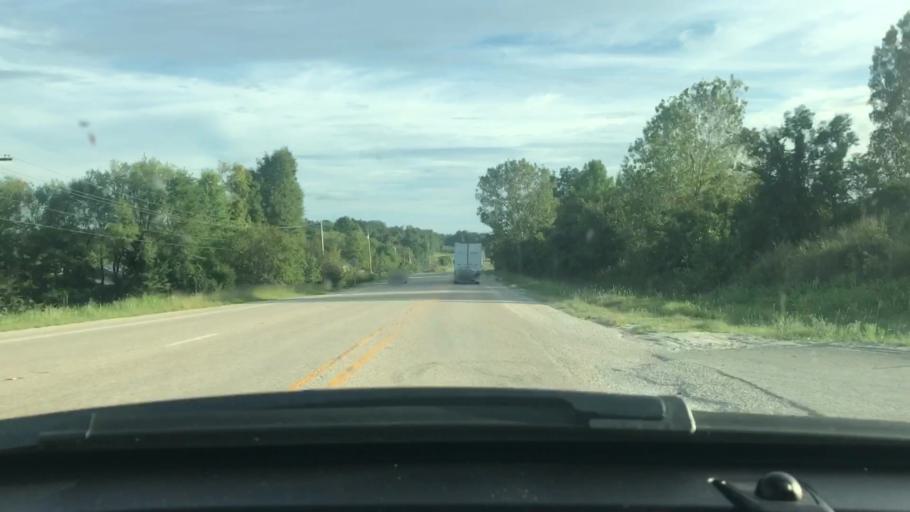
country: US
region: Arkansas
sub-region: Lawrence County
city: Hoxie
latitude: 36.1418
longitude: -91.1581
